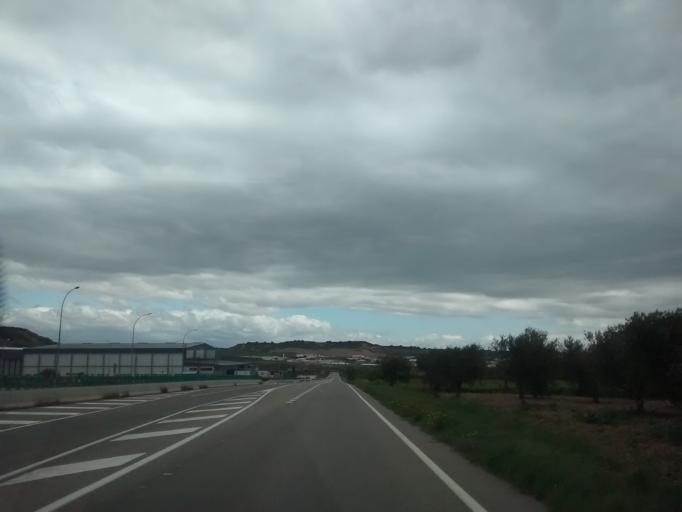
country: ES
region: La Rioja
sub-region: Provincia de La Rioja
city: Pradejon
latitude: 42.3238
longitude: -2.0916
